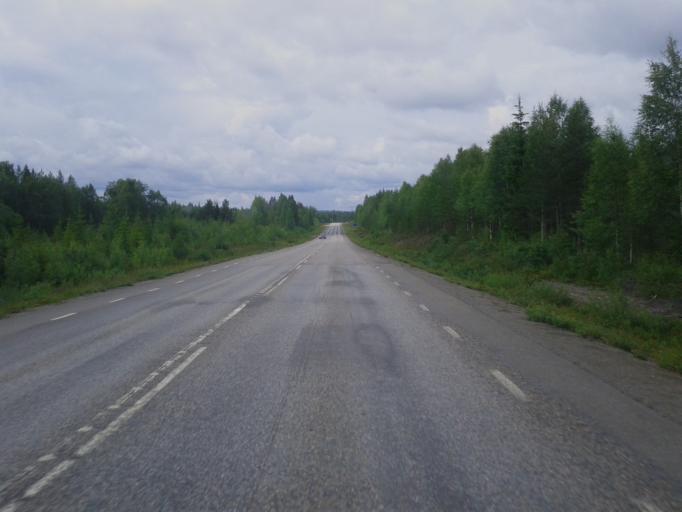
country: SE
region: Vaesterbotten
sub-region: Norsjo Kommun
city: Norsjoe
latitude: 64.9734
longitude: 19.7336
